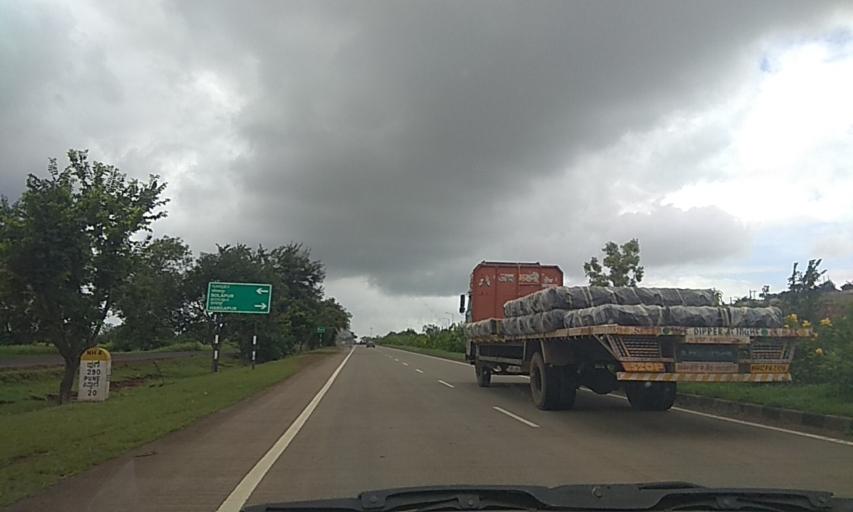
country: IN
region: Karnataka
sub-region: Belgaum
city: Sankeshwar
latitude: 16.2716
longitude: 74.4606
